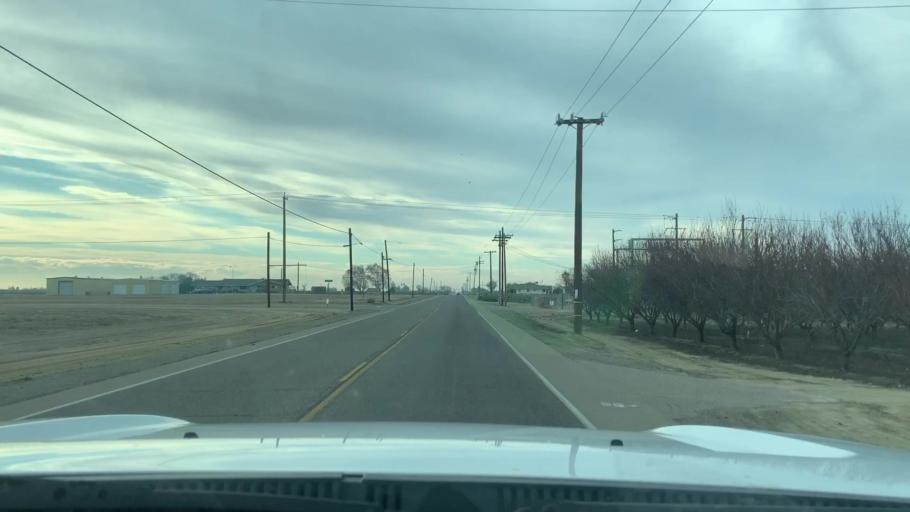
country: US
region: California
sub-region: Fresno County
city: Easton
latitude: 36.6053
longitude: -119.7721
